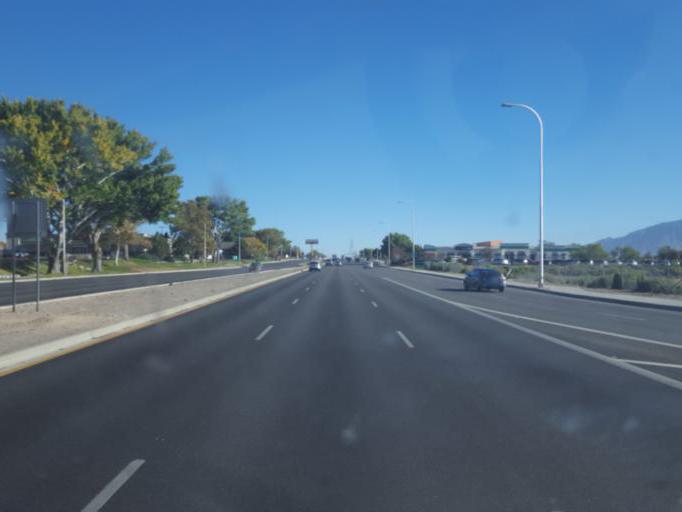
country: US
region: New Mexico
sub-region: Bernalillo County
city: Los Ranchos de Albuquerque
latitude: 35.1815
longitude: -106.6674
